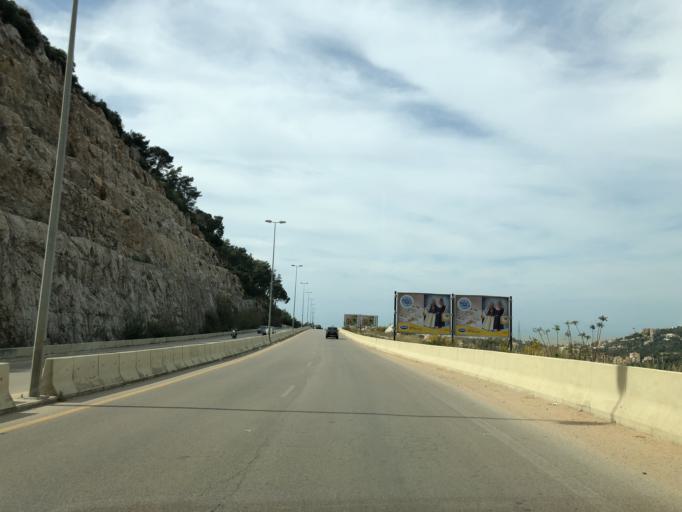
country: LB
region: Mont-Liban
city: Jdaidet el Matn
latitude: 33.8993
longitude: 35.6461
